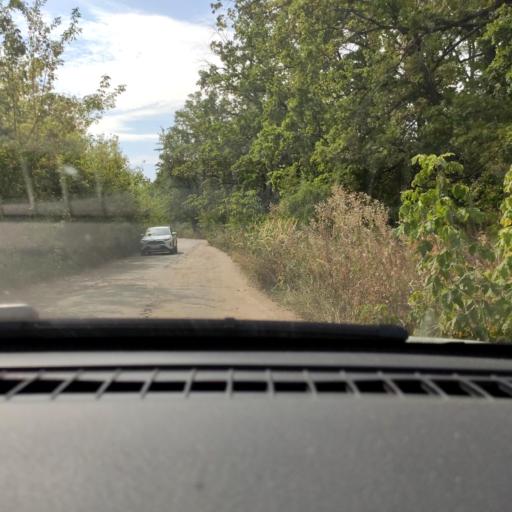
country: RU
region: Voronezj
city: Pridonskoy
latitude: 51.7457
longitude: 39.0737
